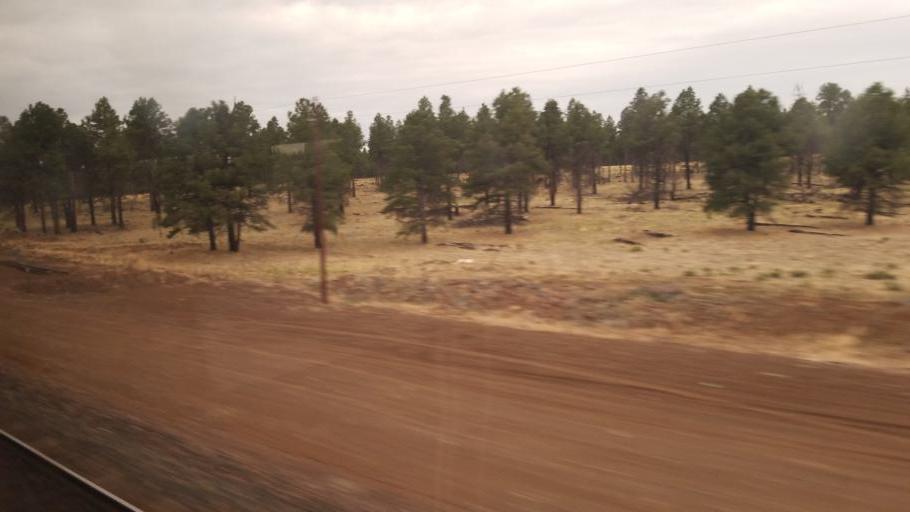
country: US
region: Arizona
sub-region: Coconino County
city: Parks
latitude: 35.2382
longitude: -112.0281
